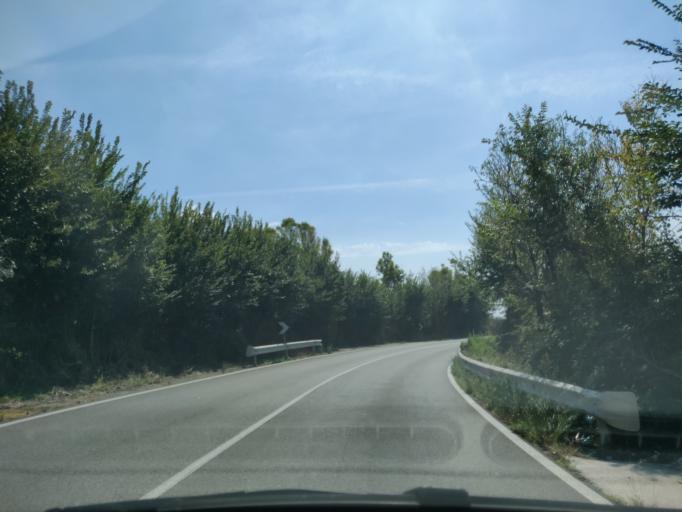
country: IT
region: Latium
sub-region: Provincia di Viterbo
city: Tarquinia
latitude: 42.2293
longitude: 11.7976
